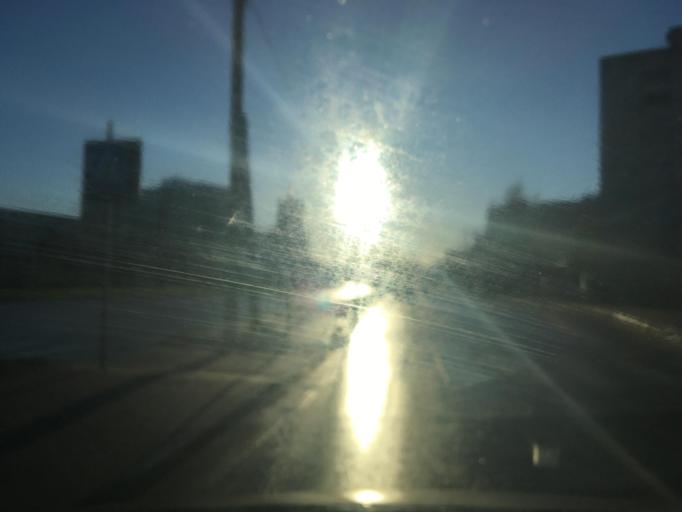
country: EE
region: Ida-Virumaa
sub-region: Narva linn
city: Narva
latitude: 59.3857
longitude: 28.1766
